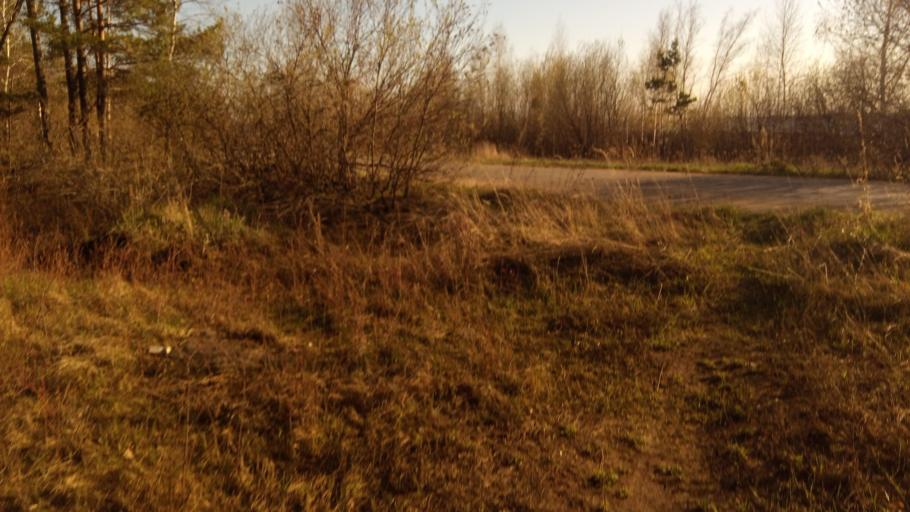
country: RU
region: Chelyabinsk
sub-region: Gorod Chelyabinsk
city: Chelyabinsk
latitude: 55.1352
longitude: 61.3274
